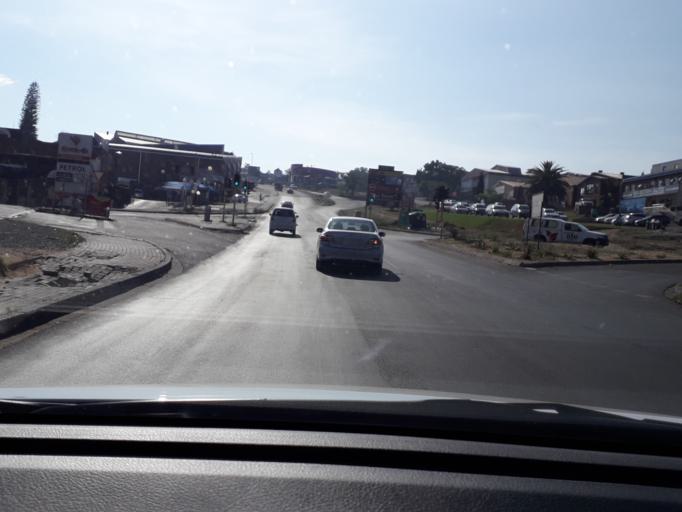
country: ZA
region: Gauteng
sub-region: City of Johannesburg Metropolitan Municipality
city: Roodepoort
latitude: -26.0800
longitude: 27.9734
